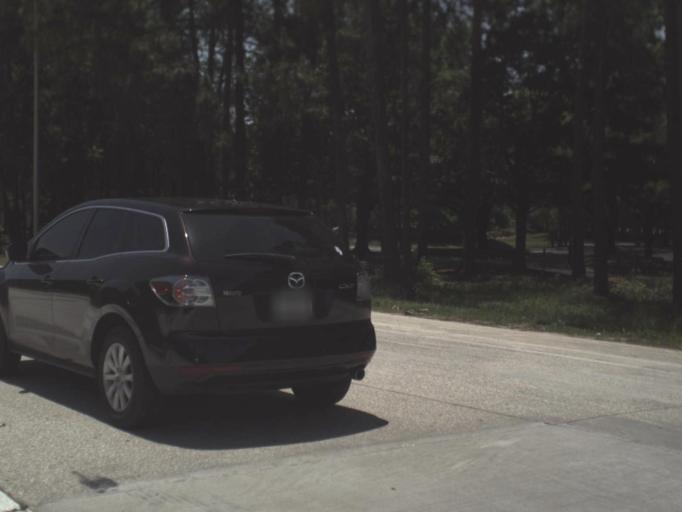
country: US
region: Florida
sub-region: Saint Johns County
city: Fruit Cove
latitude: 30.2165
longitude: -81.5686
